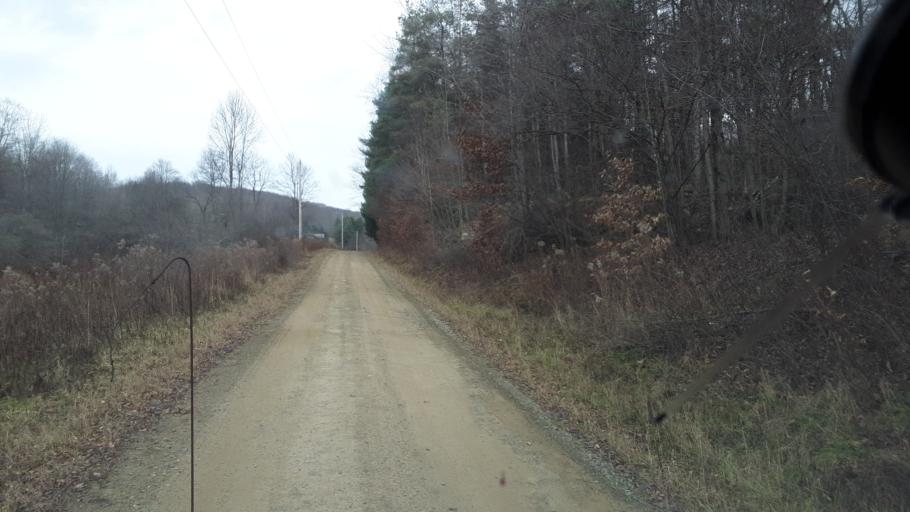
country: US
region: Pennsylvania
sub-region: Tioga County
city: Westfield
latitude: 41.9098
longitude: -77.7081
